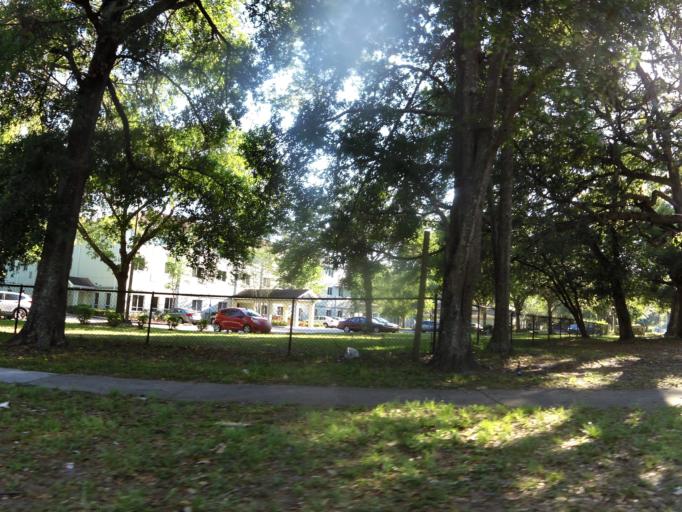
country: US
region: Florida
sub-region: Duval County
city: Jacksonville
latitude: 30.2509
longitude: -81.6239
